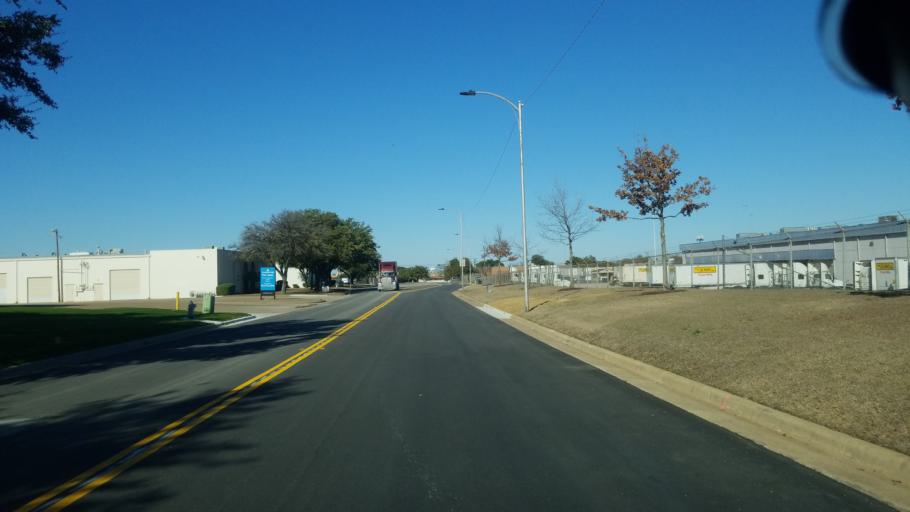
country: US
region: Texas
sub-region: Tarrant County
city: Arlington
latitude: 32.7531
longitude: -97.0542
